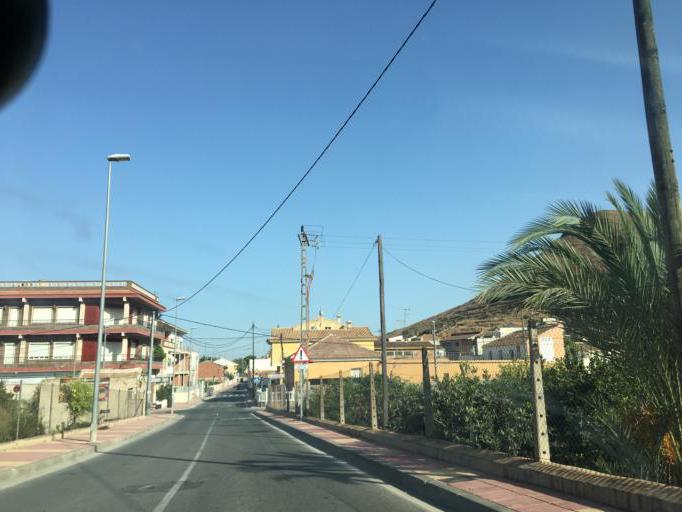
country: ES
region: Murcia
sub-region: Murcia
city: Santomera
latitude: 38.0396
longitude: -1.0831
